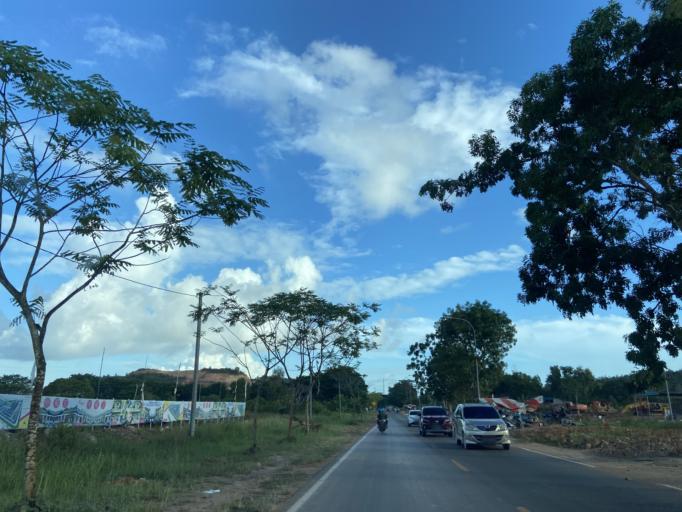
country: SG
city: Singapore
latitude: 1.0226
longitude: 104.0118
